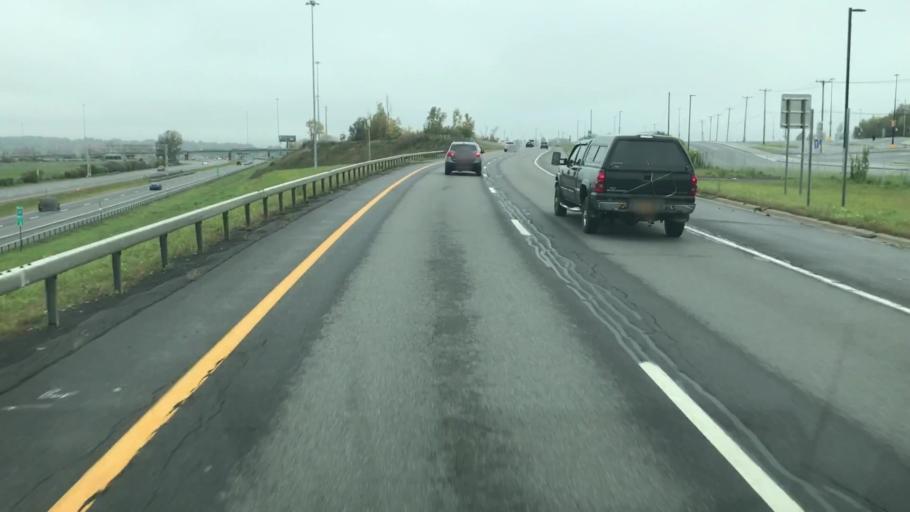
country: US
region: New York
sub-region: Onondaga County
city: Solvay
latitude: 43.0767
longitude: -76.2138
